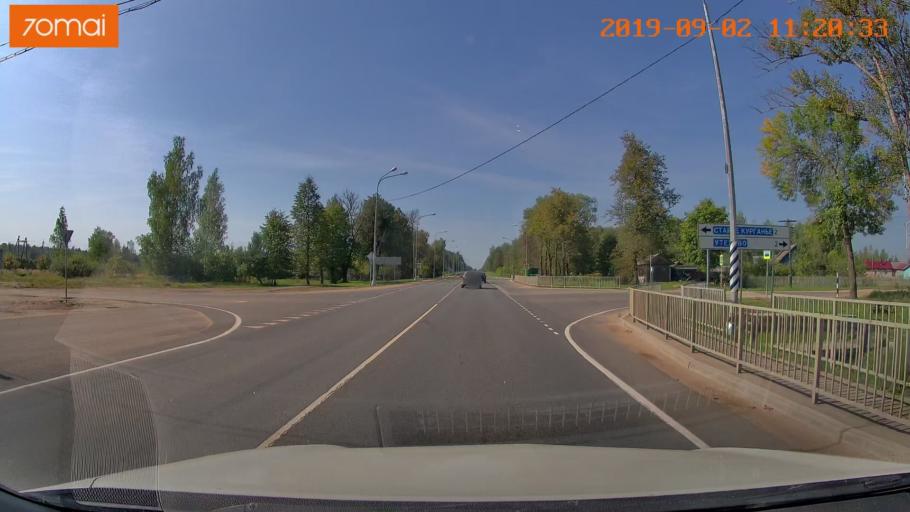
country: RU
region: Smolensk
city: Roslavl'
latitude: 54.0412
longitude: 33.0513
